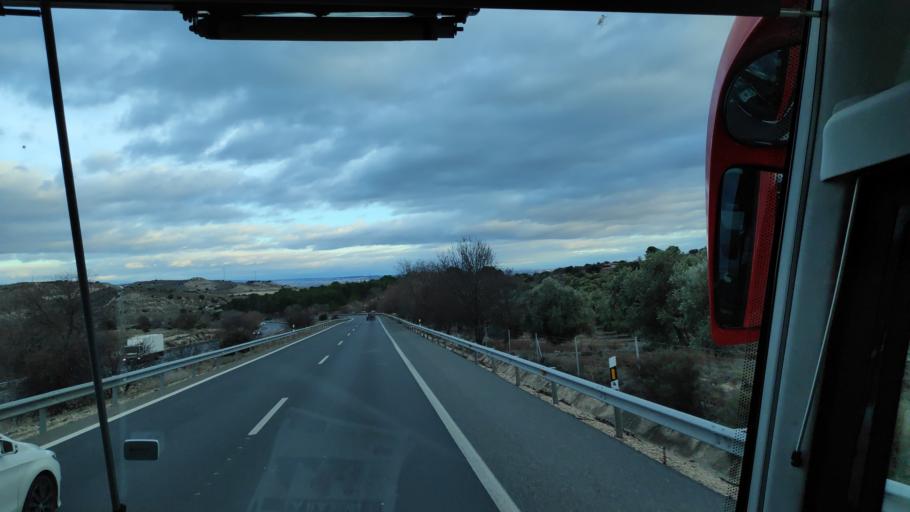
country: ES
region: Madrid
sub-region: Provincia de Madrid
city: Villarejo de Salvanes
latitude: 40.1488
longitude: -3.2298
